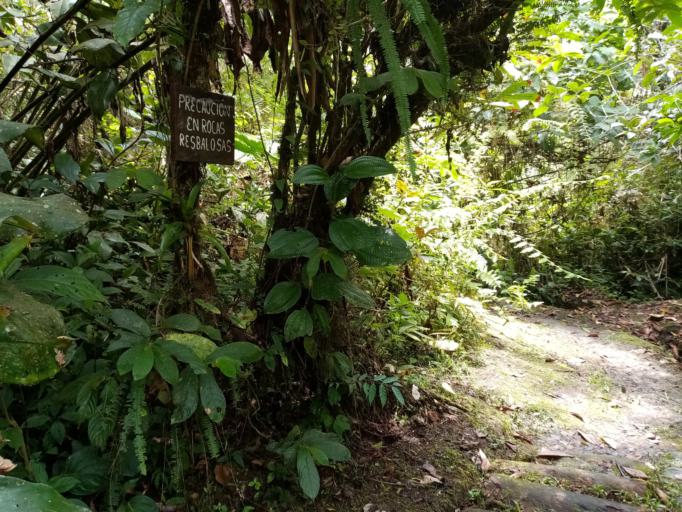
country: EC
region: Napo
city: Tena
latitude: -0.9702
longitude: -77.7985
